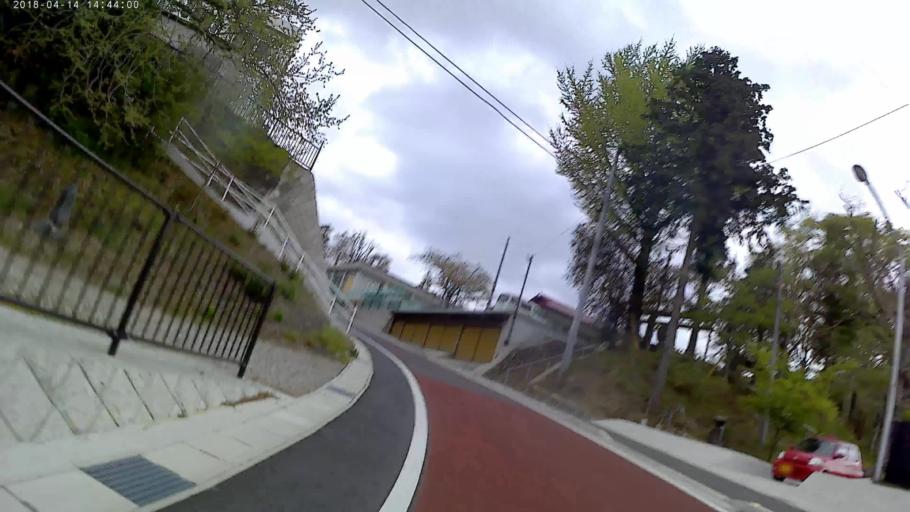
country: JP
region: Shizuoka
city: Gotemba
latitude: 35.3605
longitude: 138.9870
